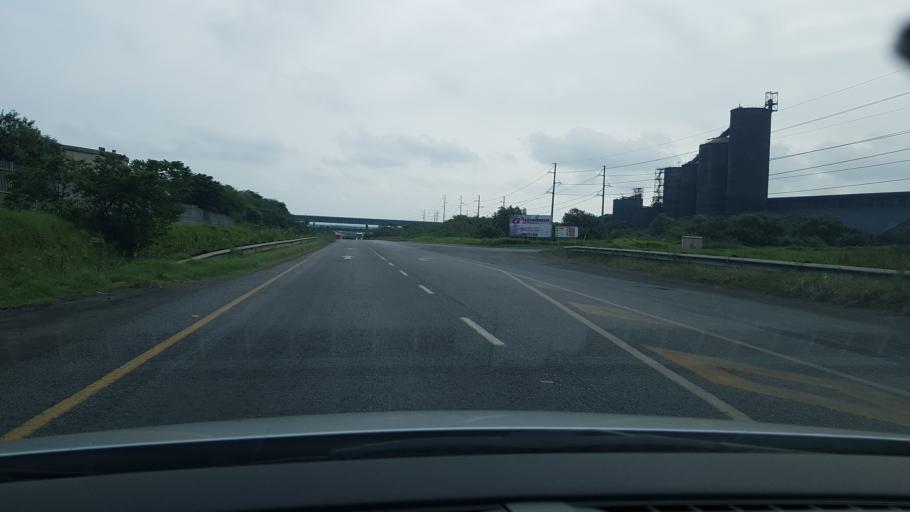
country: ZA
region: KwaZulu-Natal
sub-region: uThungulu District Municipality
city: Richards Bay
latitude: -28.7744
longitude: 32.0322
